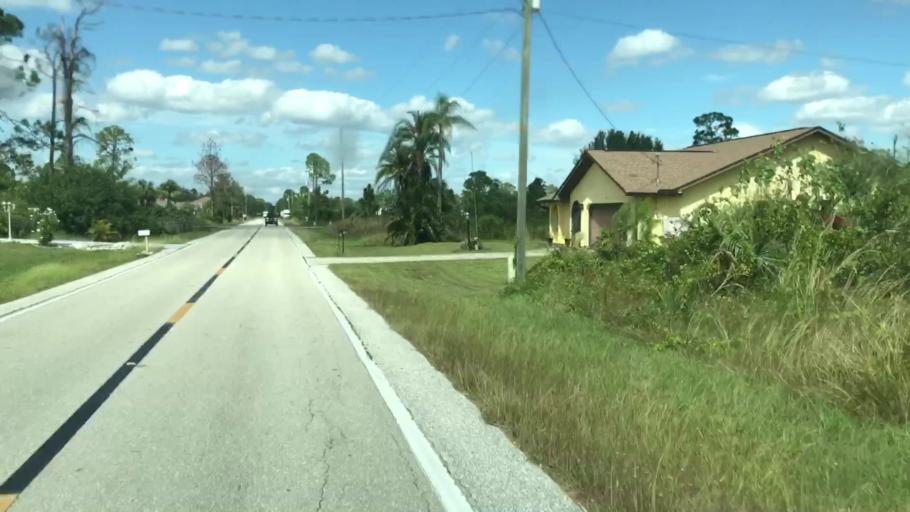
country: US
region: Florida
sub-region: Lee County
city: Lehigh Acres
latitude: 26.6311
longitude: -81.6252
